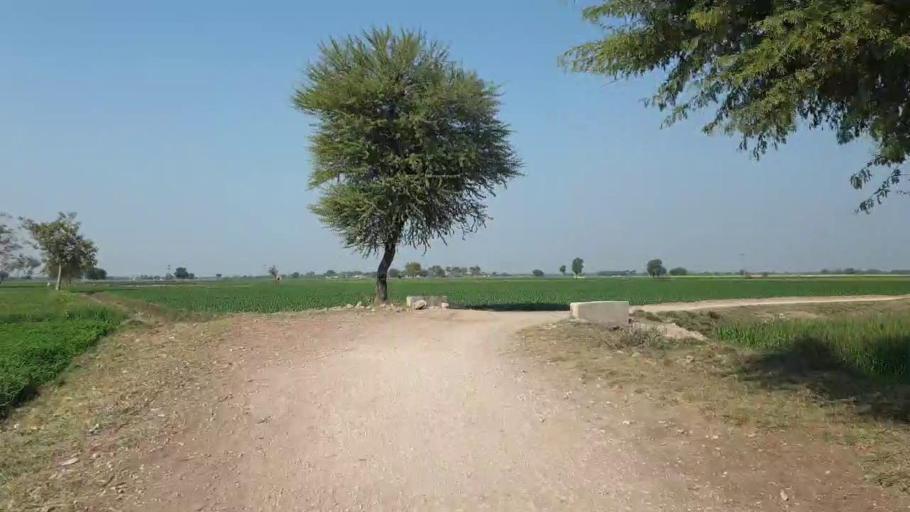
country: PK
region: Sindh
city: Hala
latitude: 25.9276
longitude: 68.4048
